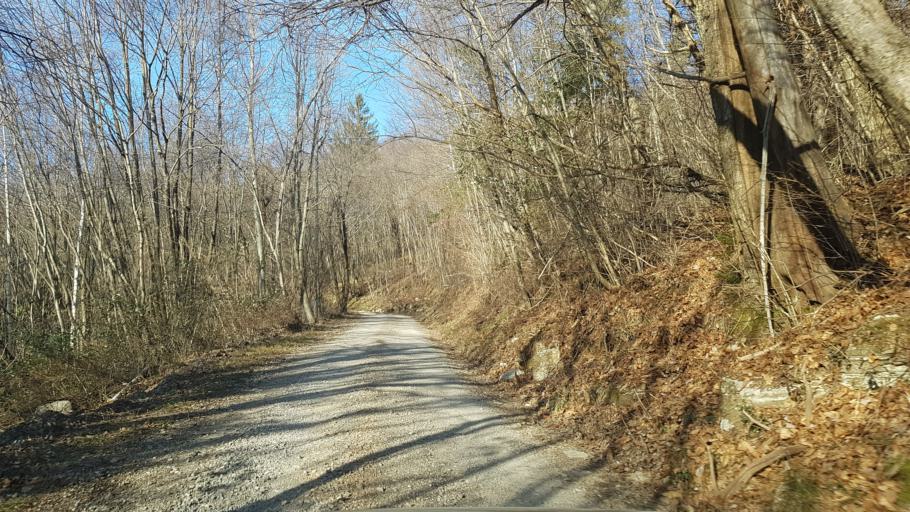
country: SI
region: Nova Gorica
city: Kromberk
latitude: 46.0113
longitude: 13.6994
